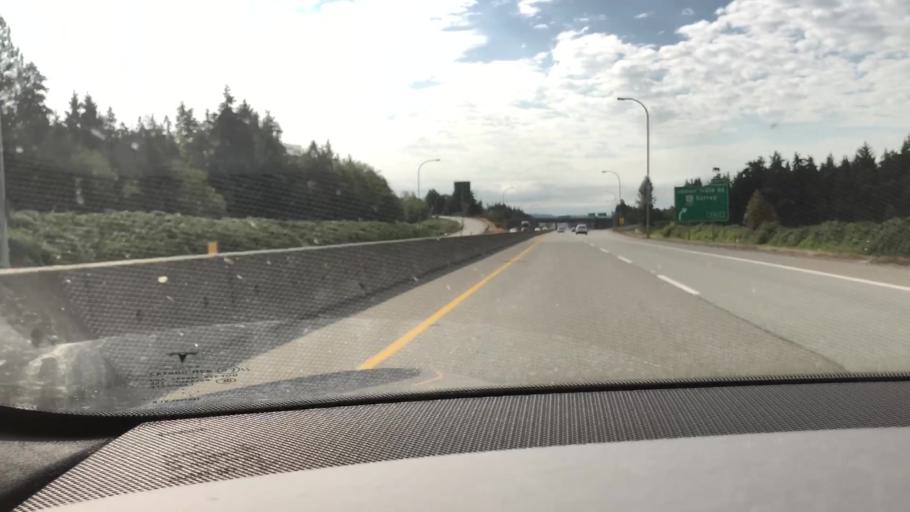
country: CA
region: British Columbia
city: Delta
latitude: 49.1074
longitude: -122.9034
